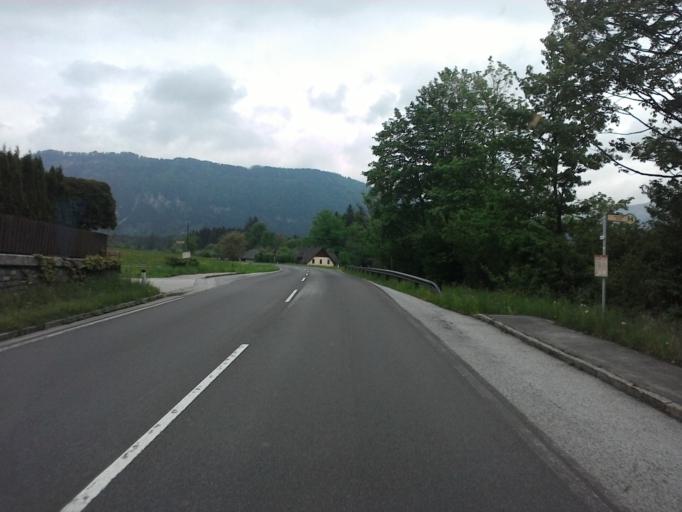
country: AT
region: Styria
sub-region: Politischer Bezirk Liezen
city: Gams bei Hieflau
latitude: 47.6406
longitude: 14.7576
